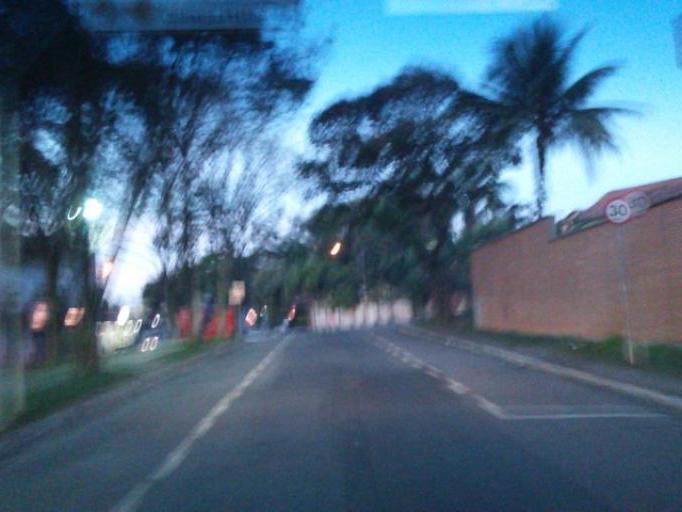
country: BR
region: Sao Paulo
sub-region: Sao Jose Dos Campos
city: Sao Jose dos Campos
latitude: -23.1951
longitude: -45.9067
